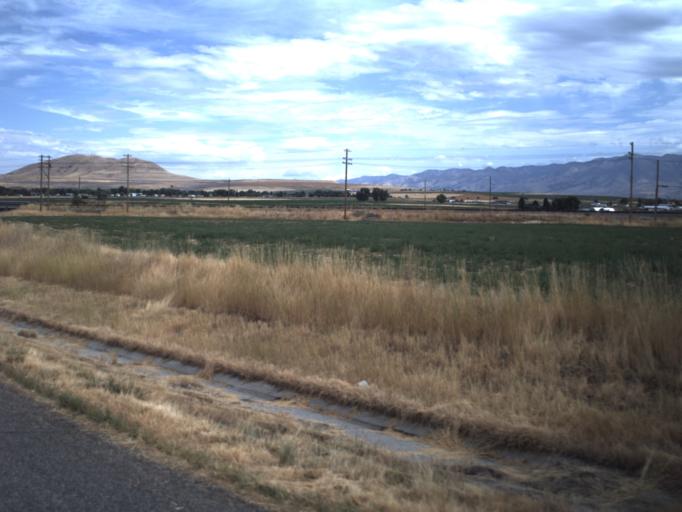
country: US
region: Utah
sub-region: Cache County
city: Benson
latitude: 41.8396
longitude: -112.0060
